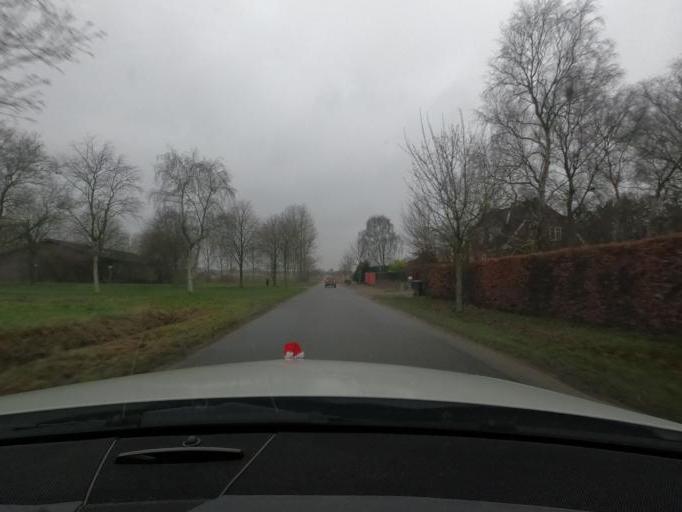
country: DK
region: South Denmark
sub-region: Haderslev Kommune
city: Haderslev
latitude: 55.1949
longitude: 9.4819
